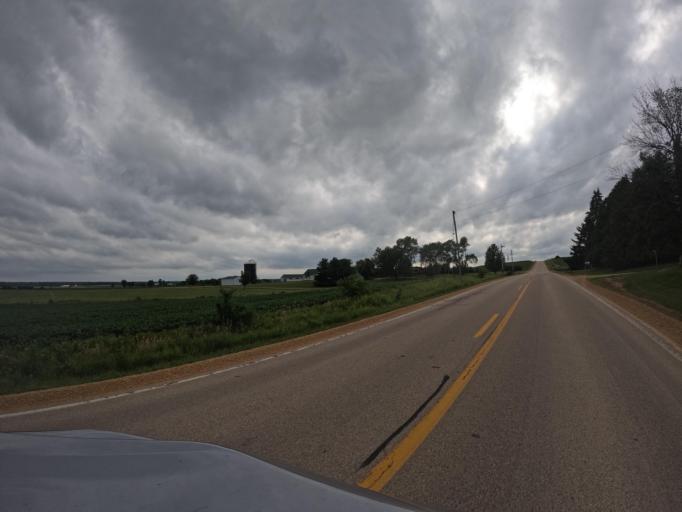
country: US
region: Iowa
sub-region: Clinton County
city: De Witt
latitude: 41.8006
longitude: -90.5254
